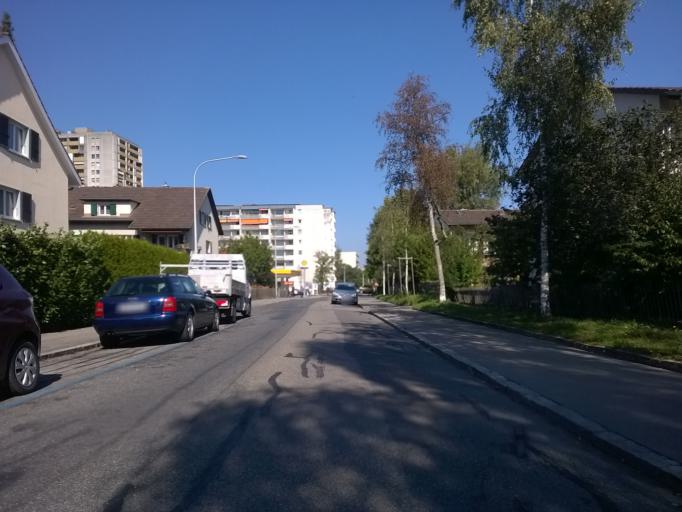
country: CH
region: Bern
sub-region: Bern-Mittelland District
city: Koniz
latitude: 46.9409
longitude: 7.3959
